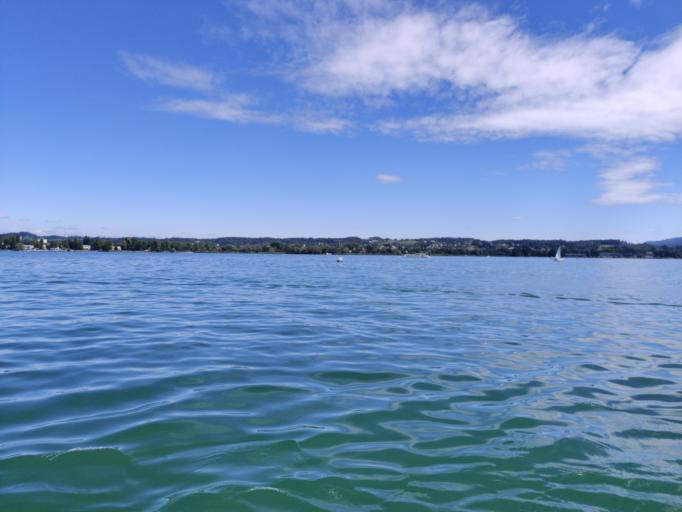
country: DE
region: Bavaria
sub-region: Swabia
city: Lindau
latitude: 47.5392
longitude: 9.6979
